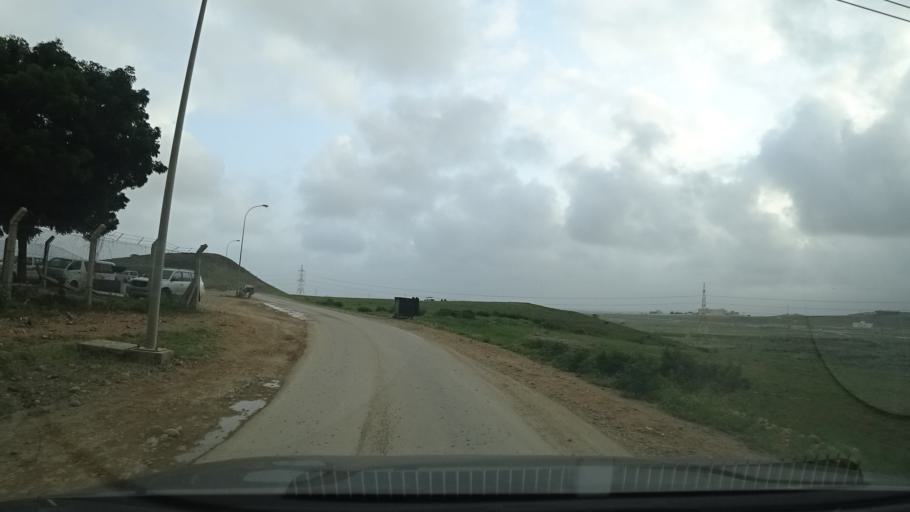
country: OM
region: Zufar
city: Salalah
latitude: 17.1198
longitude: 54.2305
